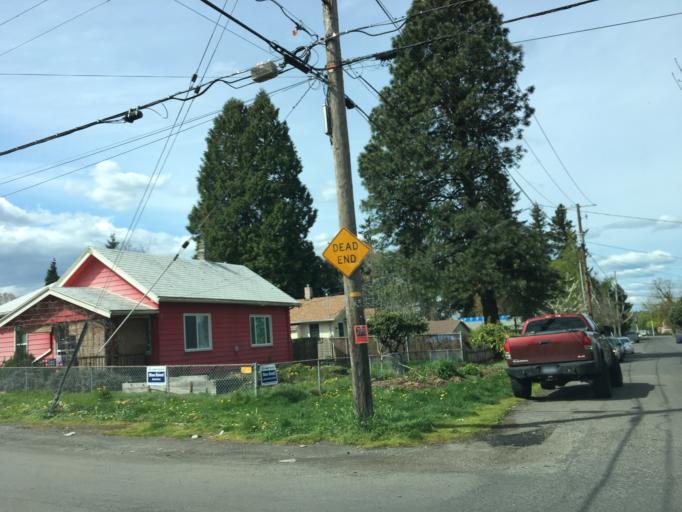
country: US
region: Oregon
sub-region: Multnomah County
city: Lents
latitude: 45.5572
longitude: -122.5608
